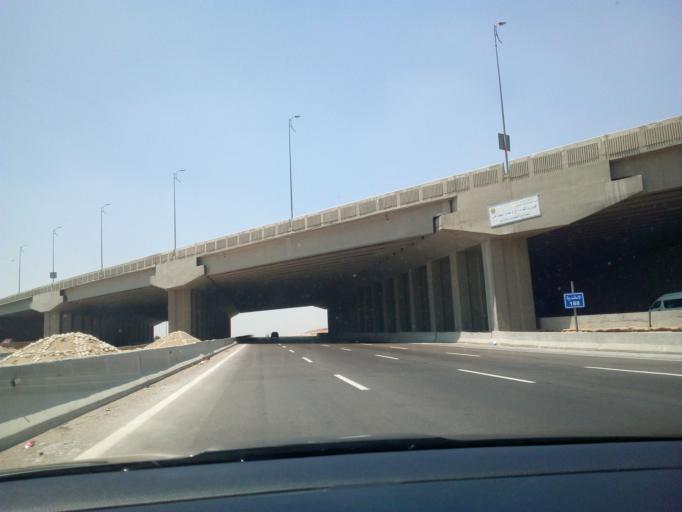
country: EG
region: Al Jizah
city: Awsim
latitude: 30.0753
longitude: 30.9286
